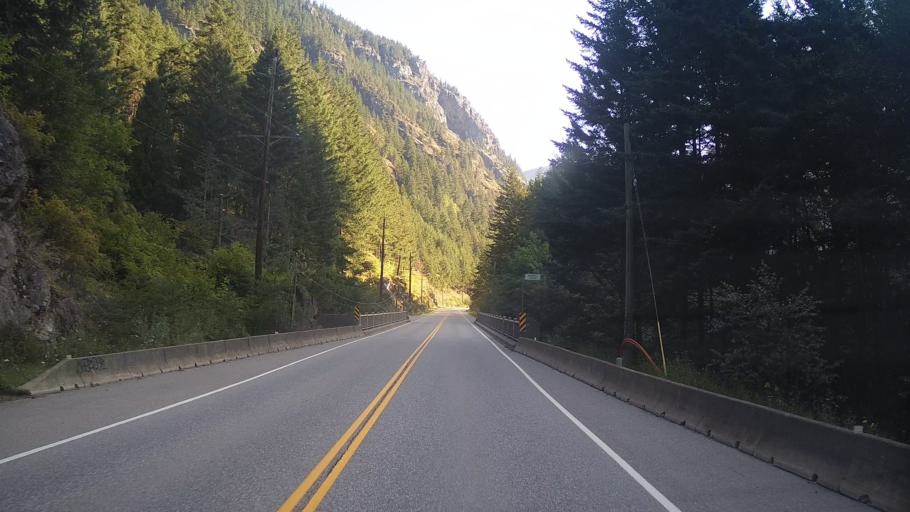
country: CA
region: British Columbia
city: Hope
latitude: 49.6119
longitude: -121.4131
